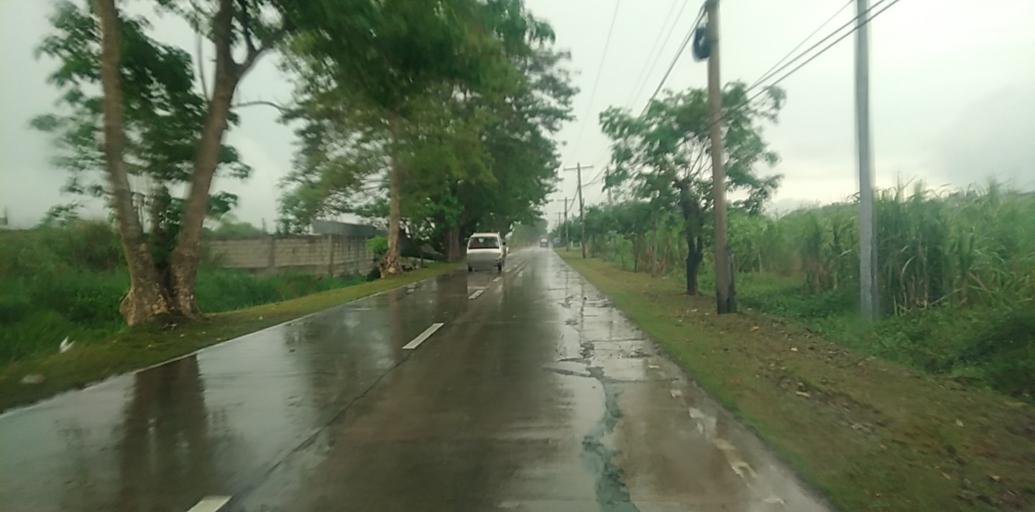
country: PH
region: Central Luzon
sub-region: Province of Pampanga
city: San Antonio
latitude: 15.1589
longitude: 120.6953
